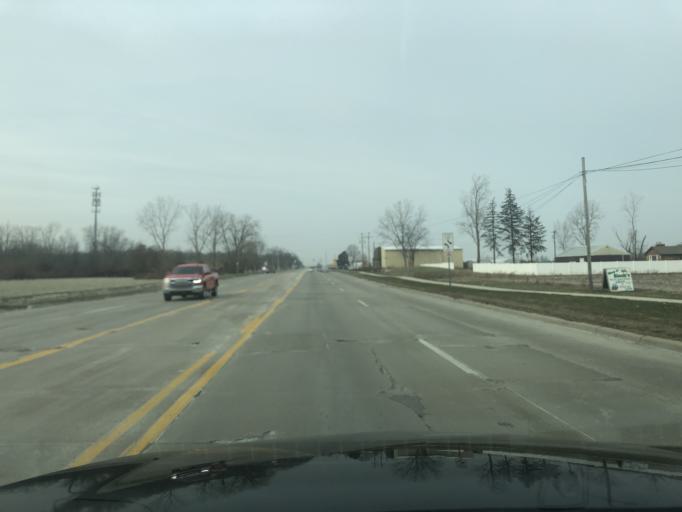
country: US
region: Michigan
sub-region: Wayne County
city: Taylor
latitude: 42.1957
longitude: -83.3168
